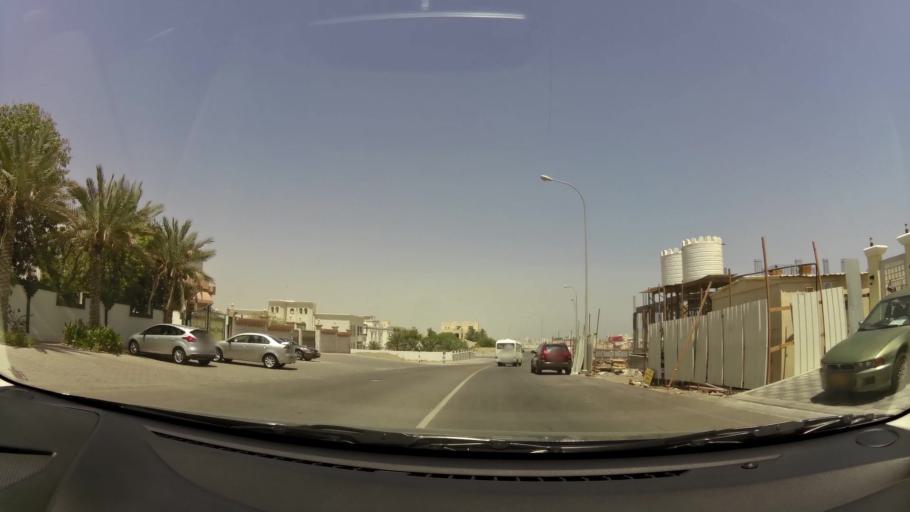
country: OM
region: Muhafazat Masqat
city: Bawshar
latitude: 23.5894
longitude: 58.4545
